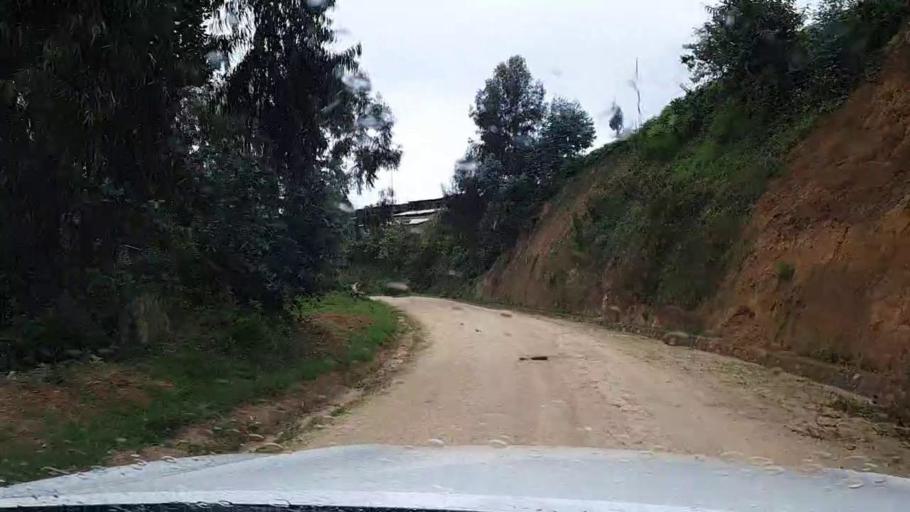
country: RW
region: Southern Province
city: Nzega
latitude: -2.3713
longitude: 29.3823
